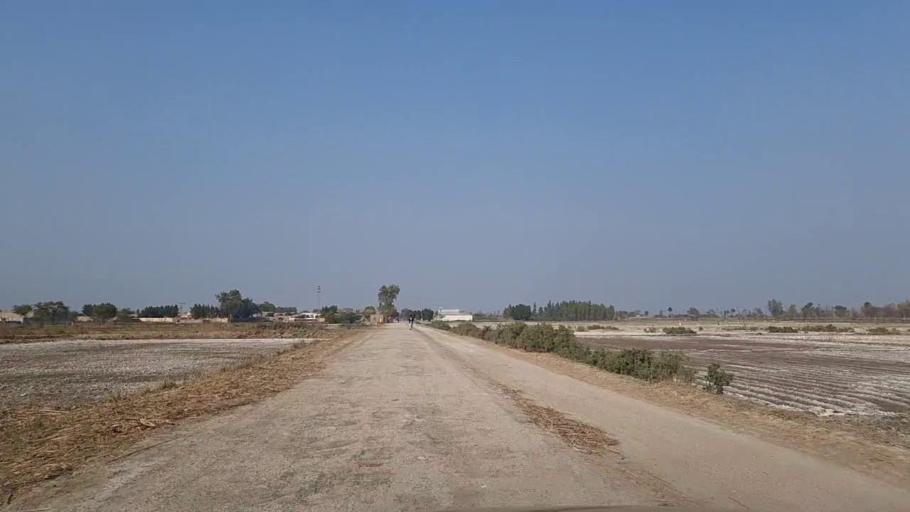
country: PK
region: Sindh
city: Daur
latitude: 26.4233
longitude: 68.4089
